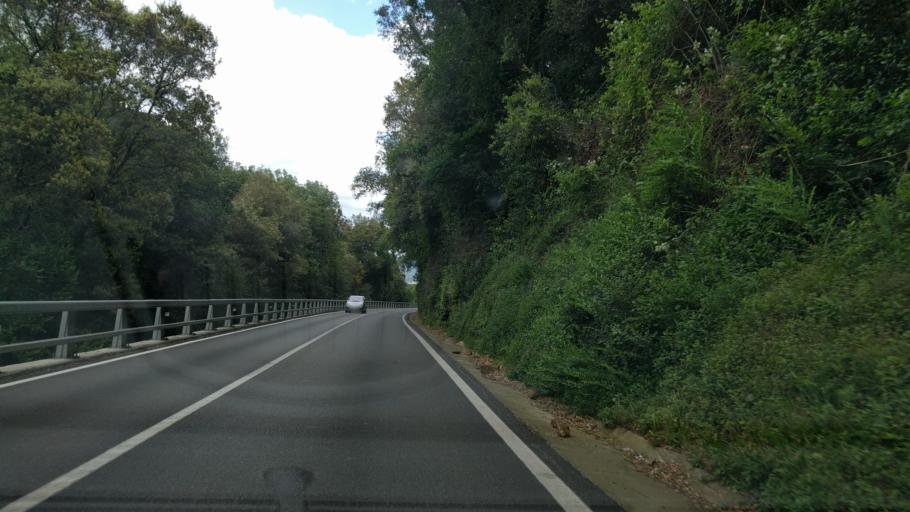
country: ES
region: Catalonia
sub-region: Provincia de Girona
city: Bescano
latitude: 41.9702
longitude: 2.7532
